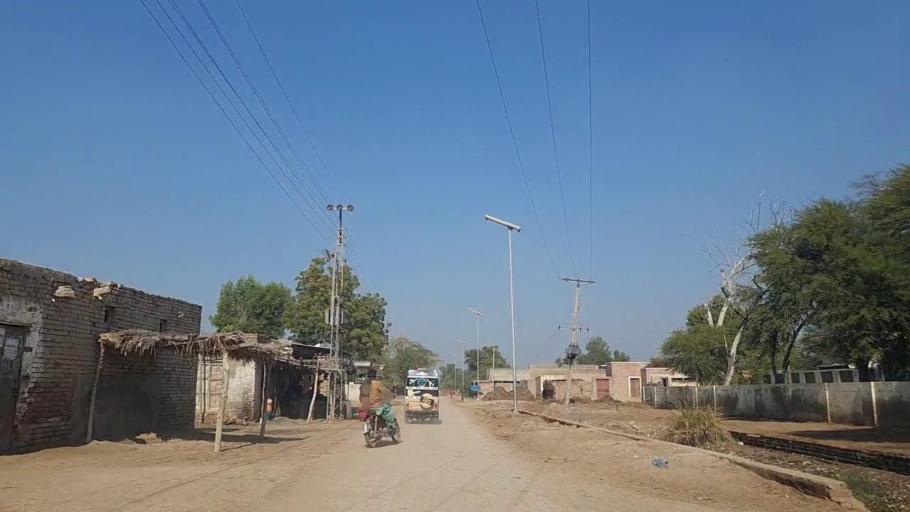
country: PK
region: Sindh
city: Nawabshah
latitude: 26.2511
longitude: 68.3411
